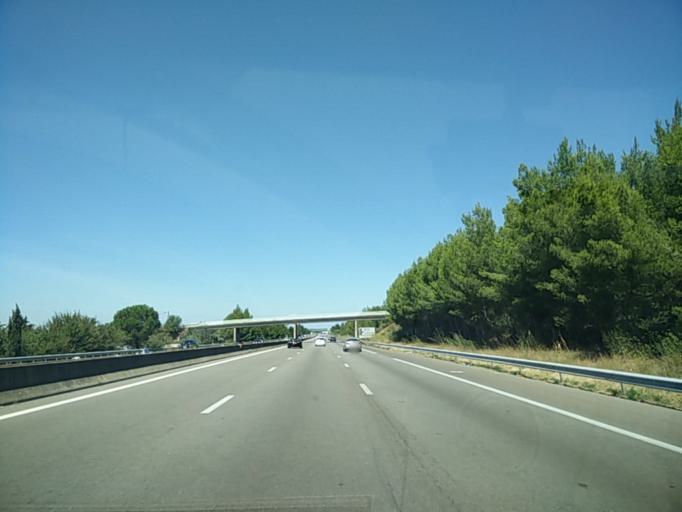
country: FR
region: Provence-Alpes-Cote d'Azur
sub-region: Departement du Vaucluse
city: Morieres-les-Avignon
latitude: 43.9567
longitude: 4.9050
